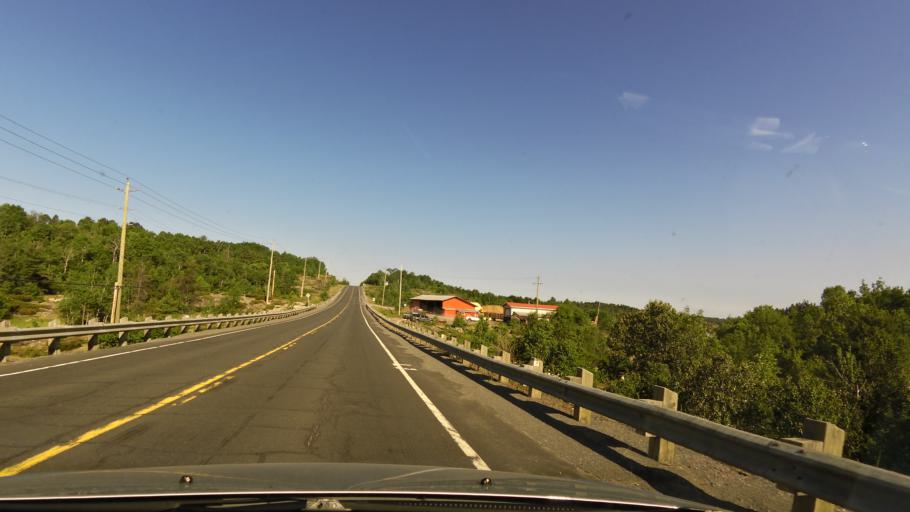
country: CA
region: Ontario
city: Greater Sudbury
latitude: 46.1049
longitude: -80.6387
